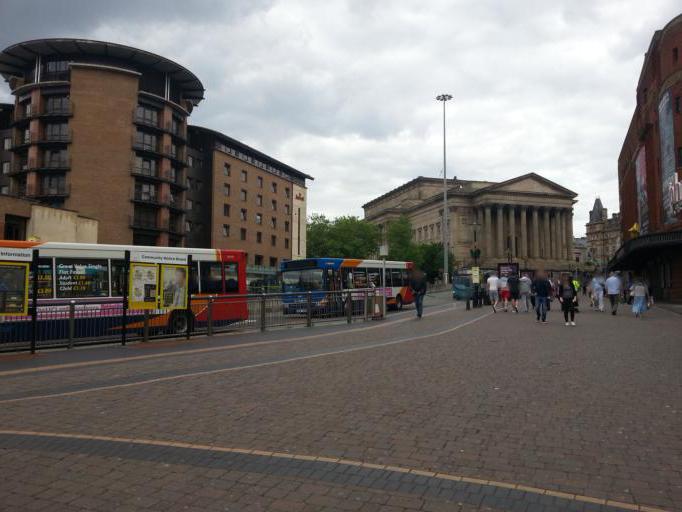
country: GB
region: England
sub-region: Liverpool
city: Liverpool
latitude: 53.4072
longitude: -2.9822
